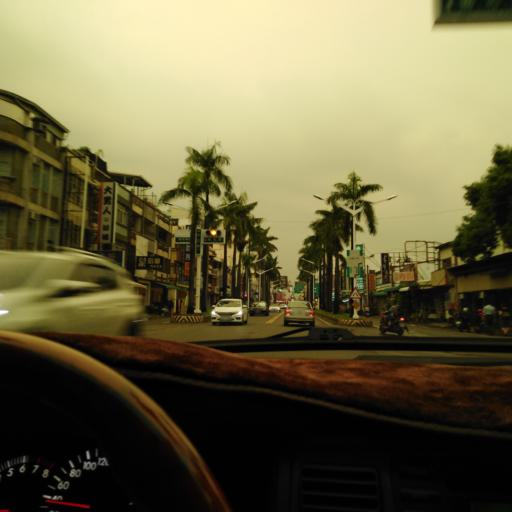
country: TW
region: Taiwan
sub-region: Pingtung
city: Pingtung
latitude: 22.6803
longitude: 120.4914
